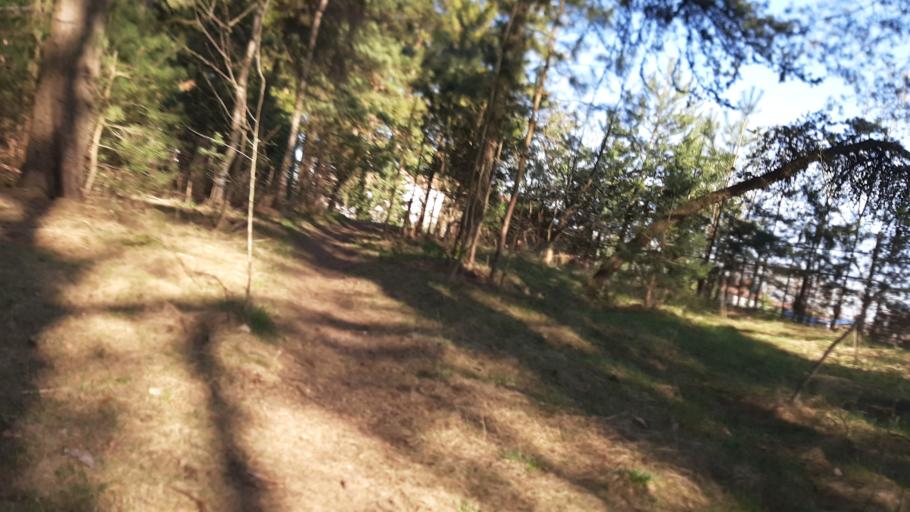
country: BY
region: Minsk
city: Minsk
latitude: 53.9517
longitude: 27.5786
